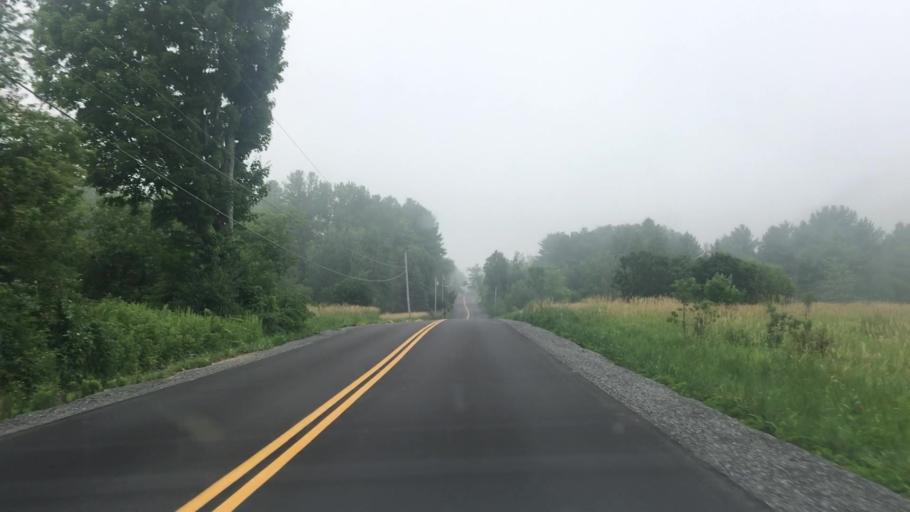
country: US
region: Maine
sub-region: Kennebec County
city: Oakland
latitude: 44.5127
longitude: -69.7113
